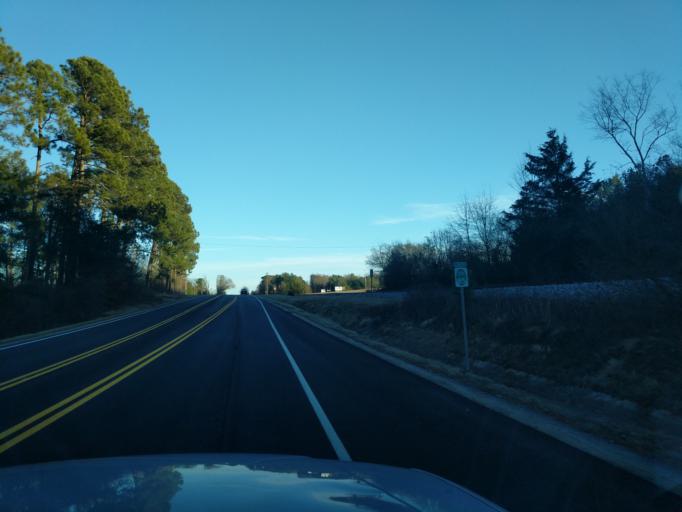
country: US
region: Georgia
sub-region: Franklin County
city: Gumlog
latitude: 34.5113
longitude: -83.2200
